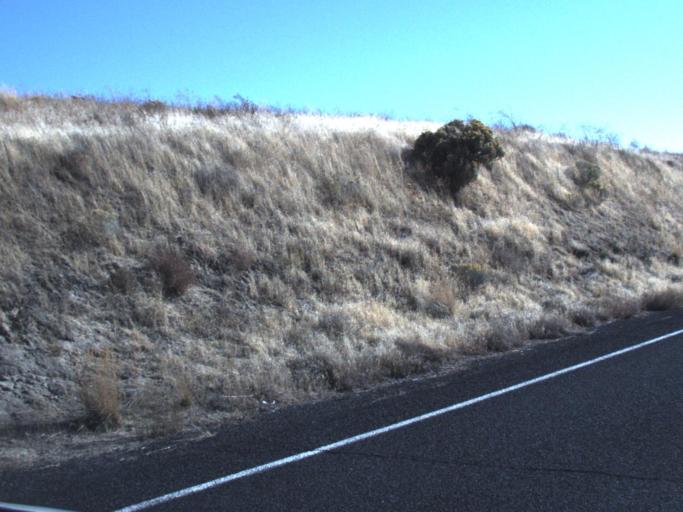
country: US
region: Washington
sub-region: Franklin County
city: Connell
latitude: 46.7032
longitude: -118.5279
